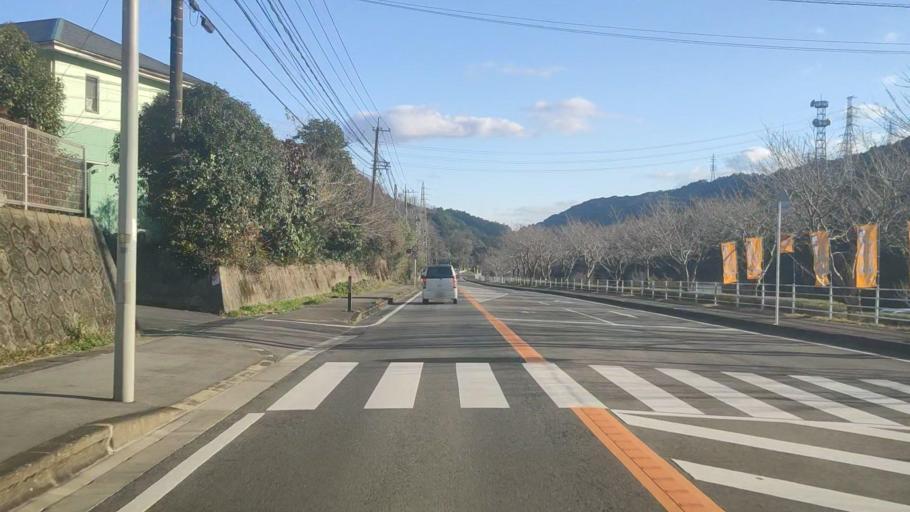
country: JP
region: Saga Prefecture
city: Saga-shi
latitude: 33.3392
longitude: 130.2583
